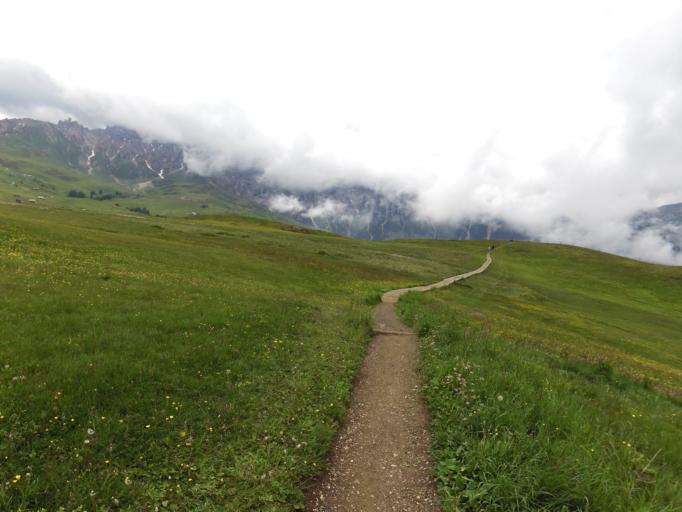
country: IT
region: Trentino-Alto Adige
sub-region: Bolzano
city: Siusi
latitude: 46.5266
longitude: 11.6187
